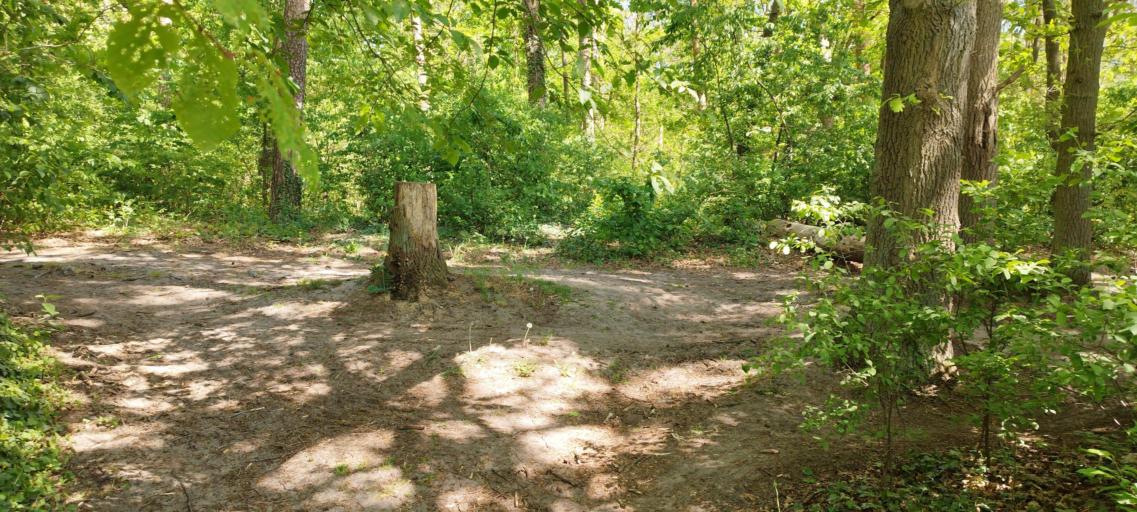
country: DE
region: Brandenburg
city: Furstenwalde
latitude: 52.3900
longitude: 14.0253
